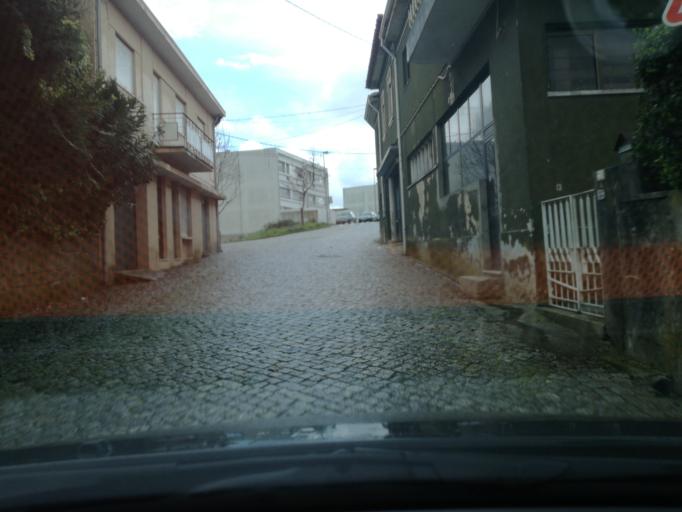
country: PT
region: Porto
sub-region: Valongo
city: Ermesinde
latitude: 41.2421
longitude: -8.5482
